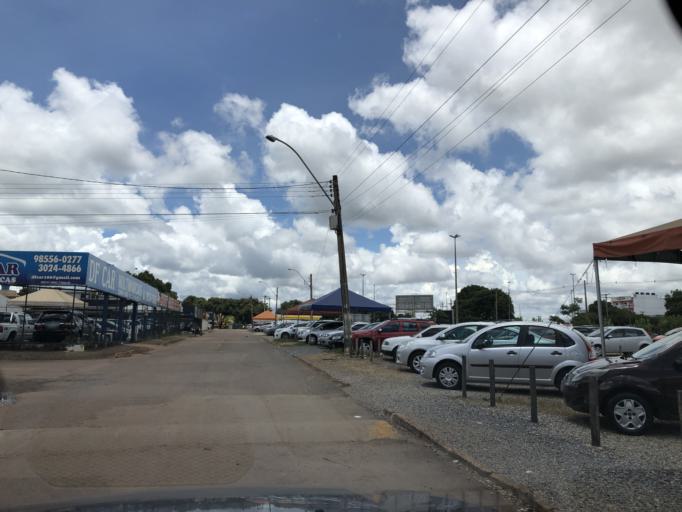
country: BR
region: Federal District
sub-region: Brasilia
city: Brasilia
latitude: -15.7992
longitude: -48.1215
